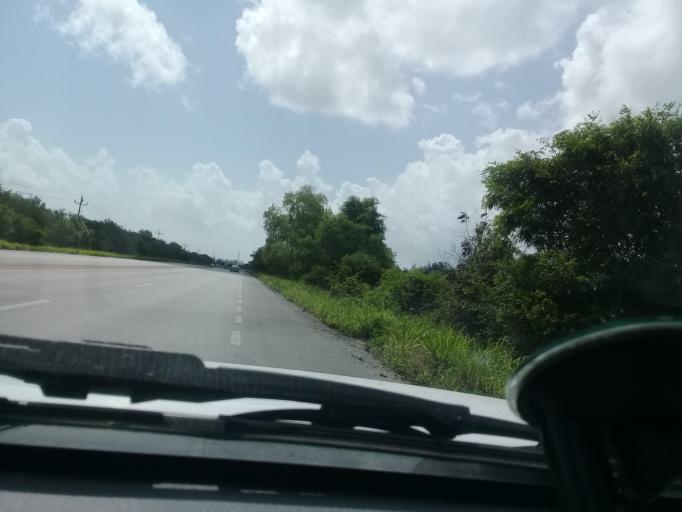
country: MX
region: Veracruz
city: Moralillo
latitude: 22.2127
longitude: -97.9695
